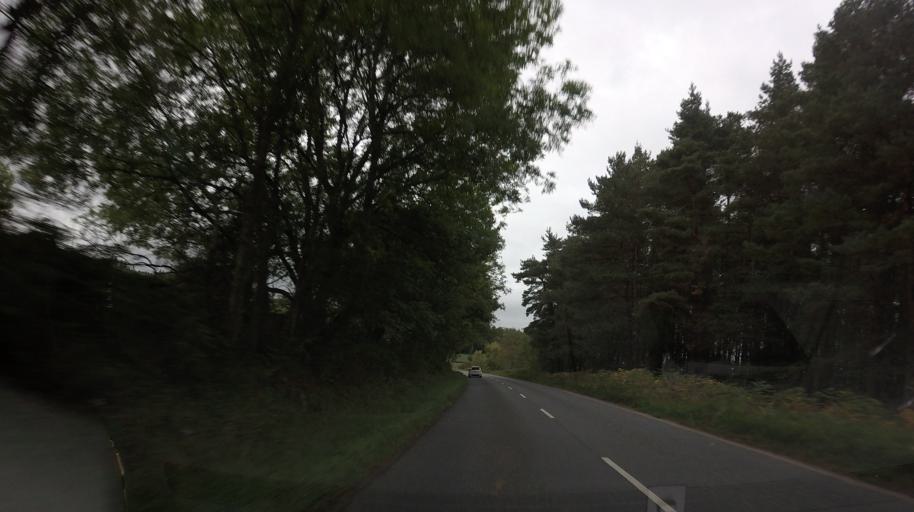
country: GB
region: Scotland
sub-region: Aberdeenshire
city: Banchory
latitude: 57.1169
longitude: -2.4262
